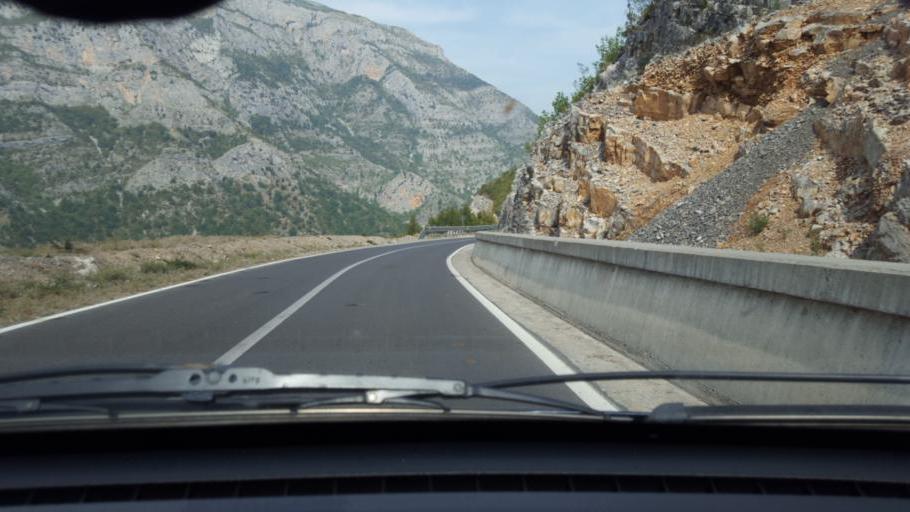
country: AL
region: Shkoder
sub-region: Rrethi i Malesia e Madhe
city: Kastrat
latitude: 42.4172
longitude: 19.5006
